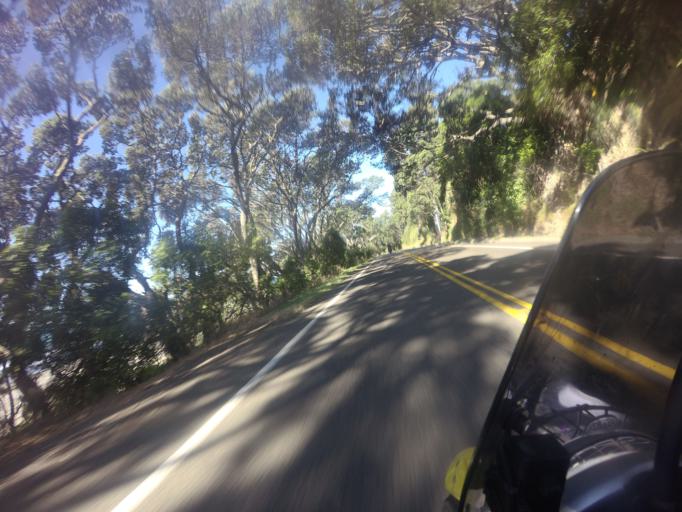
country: NZ
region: Bay of Plenty
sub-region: Opotiki District
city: Opotiki
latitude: -37.9916
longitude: 177.2206
